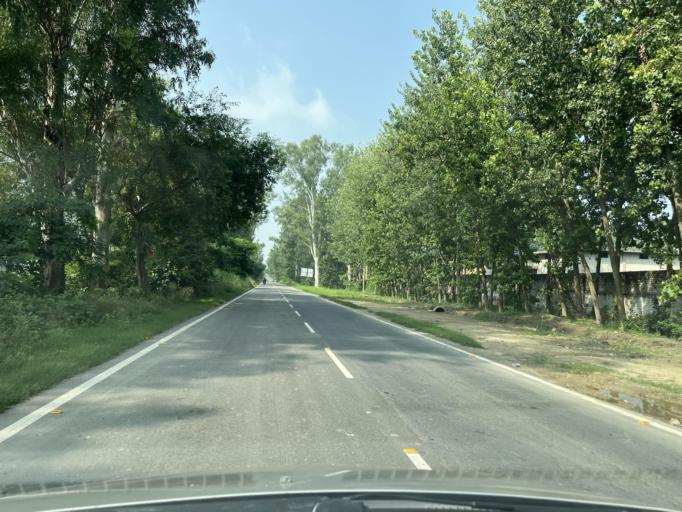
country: IN
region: Uttarakhand
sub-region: Udham Singh Nagar
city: Bazpur
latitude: 29.1761
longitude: 79.1727
